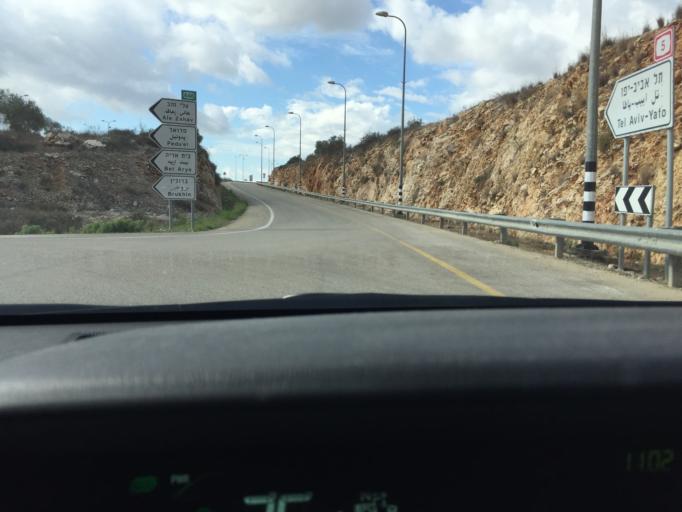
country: PS
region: West Bank
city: Sartah
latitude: 32.0939
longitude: 35.1069
